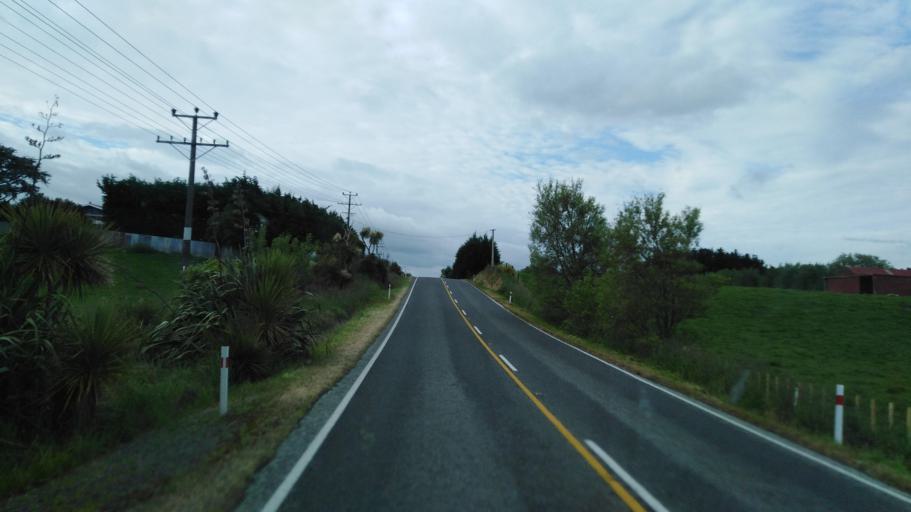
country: NZ
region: Manawatu-Wanganui
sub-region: Rangitikei District
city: Bulls
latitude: -40.1203
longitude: 175.3558
